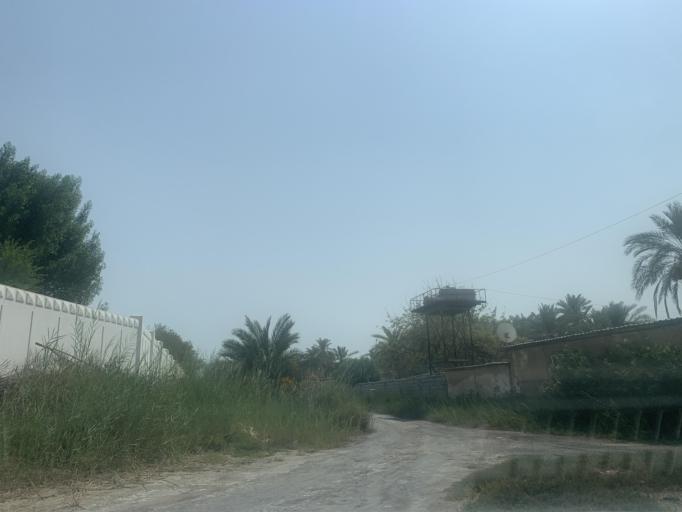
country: BH
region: Central Governorate
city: Madinat Hamad
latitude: 26.1687
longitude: 50.4510
